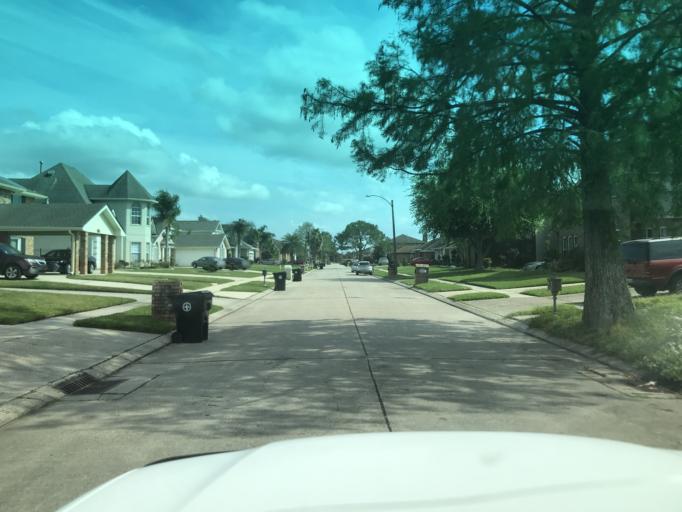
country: US
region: Louisiana
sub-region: Saint Bernard Parish
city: Chalmette
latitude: 30.0346
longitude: -89.9560
